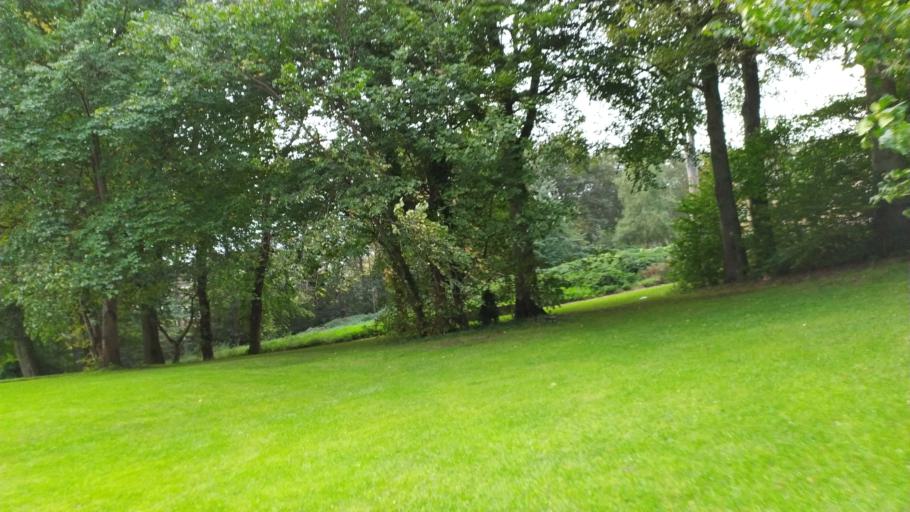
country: GB
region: England
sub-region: City and Borough of Leeds
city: Leeds
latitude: 53.8199
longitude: -1.5911
